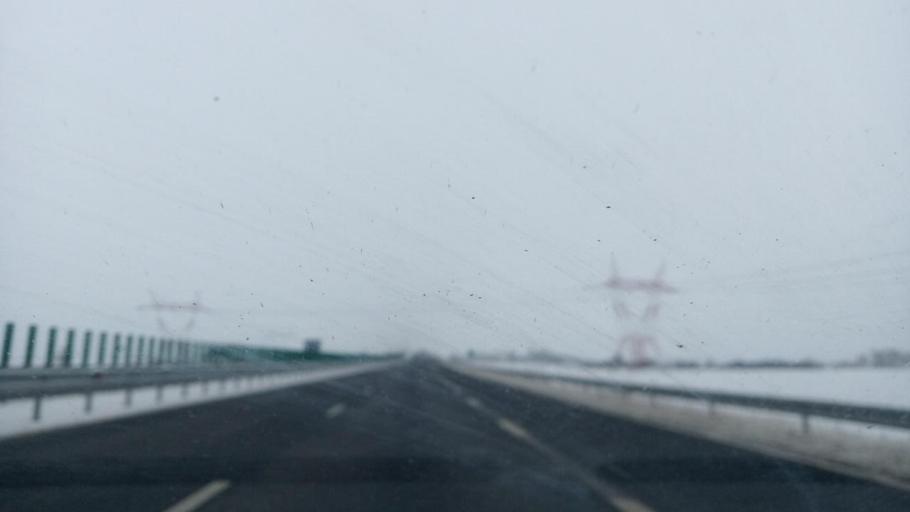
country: RO
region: Bacau
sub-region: Comuna Letea Veche
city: Holt
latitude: 46.5951
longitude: 26.9608
